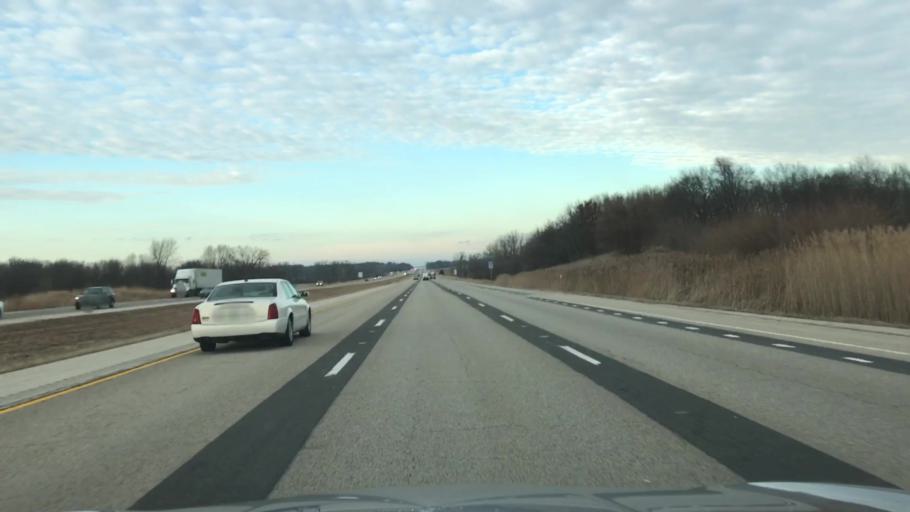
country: US
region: Illinois
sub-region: Logan County
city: Lincoln
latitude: 40.1185
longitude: -89.4164
